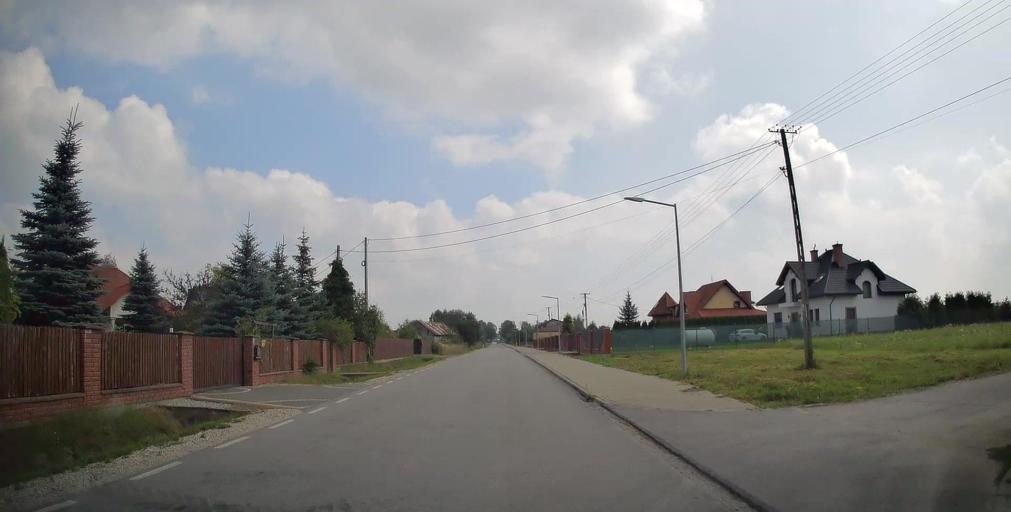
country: PL
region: Masovian Voivodeship
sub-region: Powiat bialobrzeski
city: Sucha
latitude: 51.6104
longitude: 20.9735
